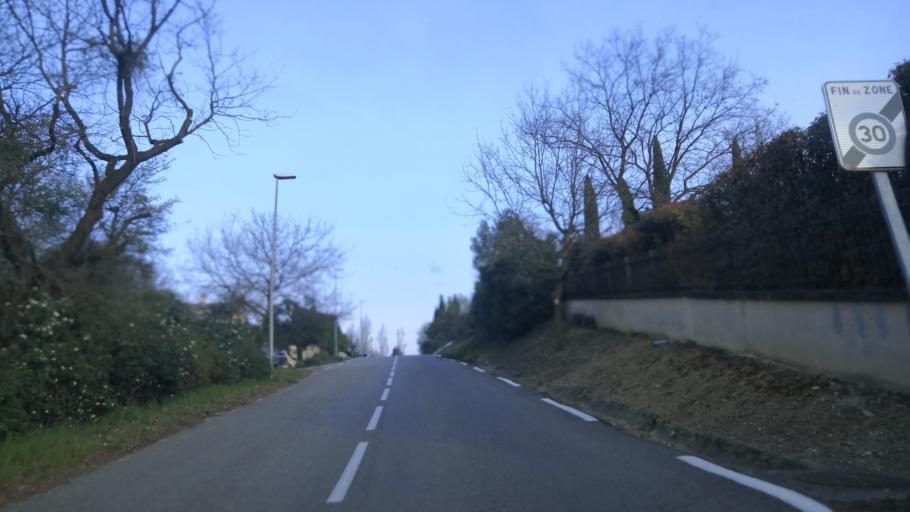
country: FR
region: Rhone-Alpes
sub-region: Departement de la Drome
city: Montelimar
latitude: 44.5715
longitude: 4.7620
